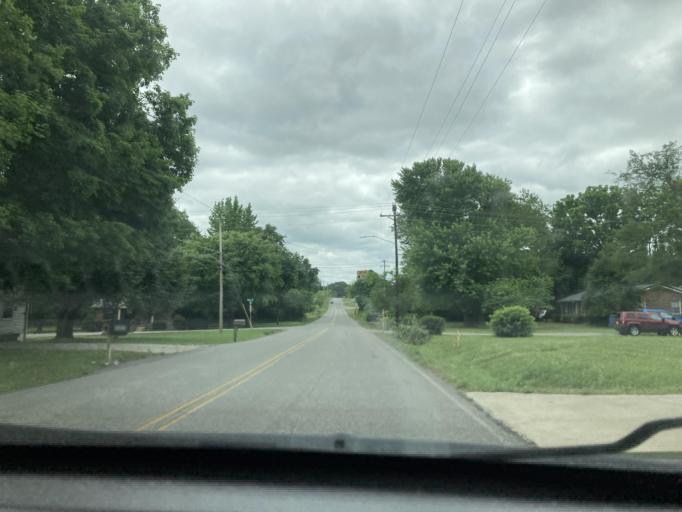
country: US
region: Tennessee
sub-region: Dickson County
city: Dickson
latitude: 36.0904
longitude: -87.3800
